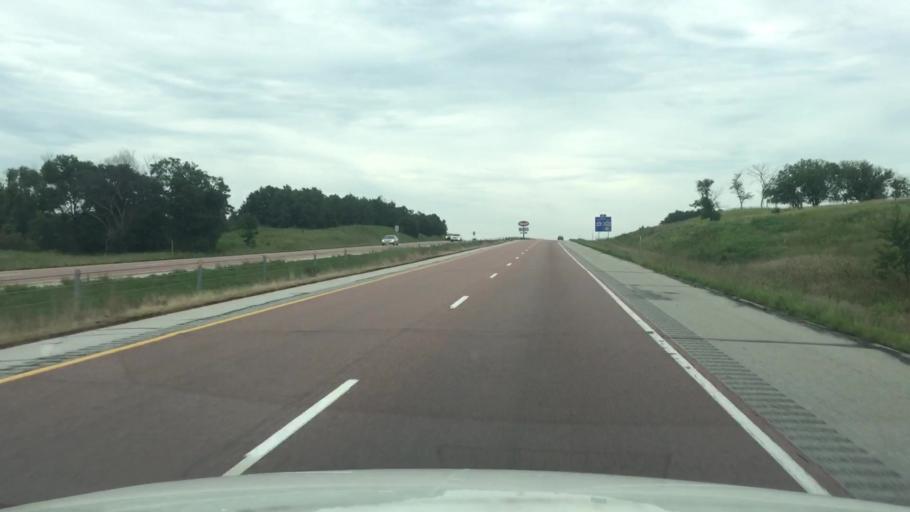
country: US
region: Iowa
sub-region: Clarke County
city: Osceola
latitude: 41.1858
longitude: -93.7847
